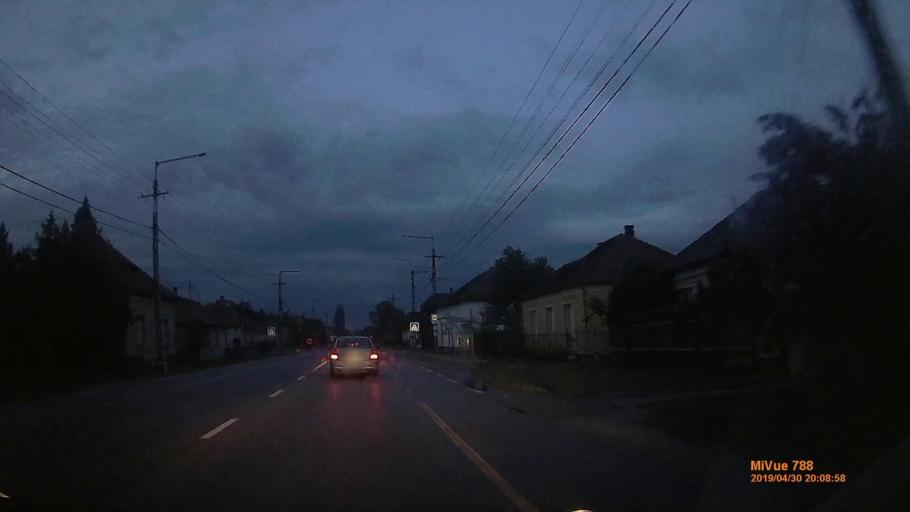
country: HU
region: Pest
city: Abony
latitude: 47.1839
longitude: 20.0500
